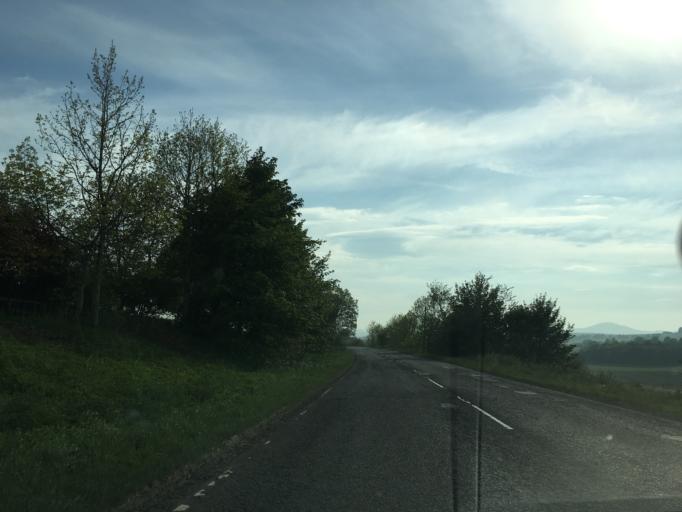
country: GB
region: Scotland
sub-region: The Scottish Borders
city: West Linton
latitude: 55.7529
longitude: -3.2788
